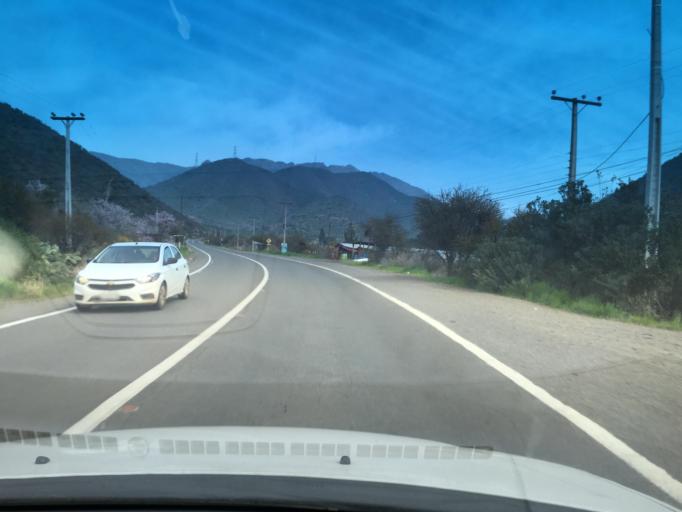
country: CL
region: Santiago Metropolitan
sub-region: Provincia de Chacabuco
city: Lampa
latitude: -33.0753
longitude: -70.9387
